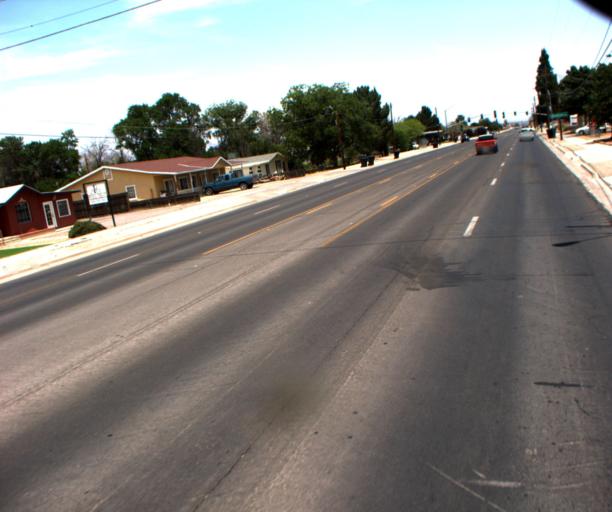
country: US
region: Arizona
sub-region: Graham County
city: Thatcher
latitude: 32.8491
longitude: -109.7651
